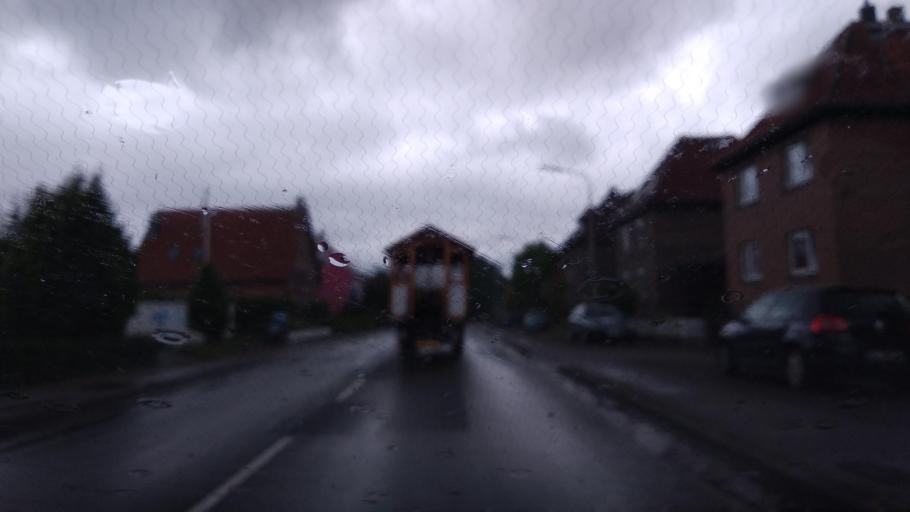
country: DE
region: Lower Saxony
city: Stadthagen
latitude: 52.3104
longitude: 9.1950
